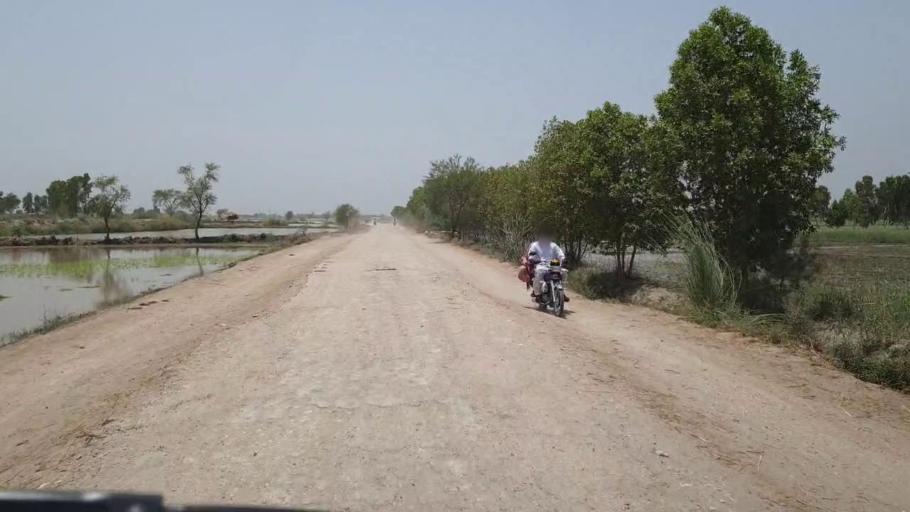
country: PK
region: Sindh
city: Daur
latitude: 26.4580
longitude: 68.1542
